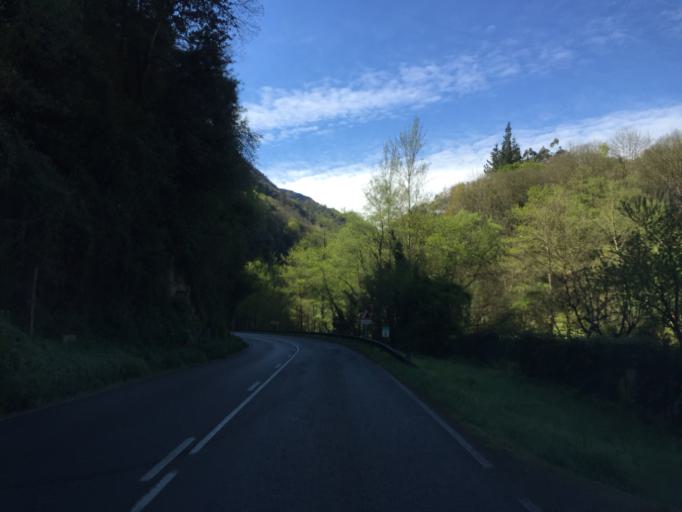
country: ES
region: Asturias
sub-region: Province of Asturias
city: Proaza
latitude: 43.2879
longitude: -5.9834
